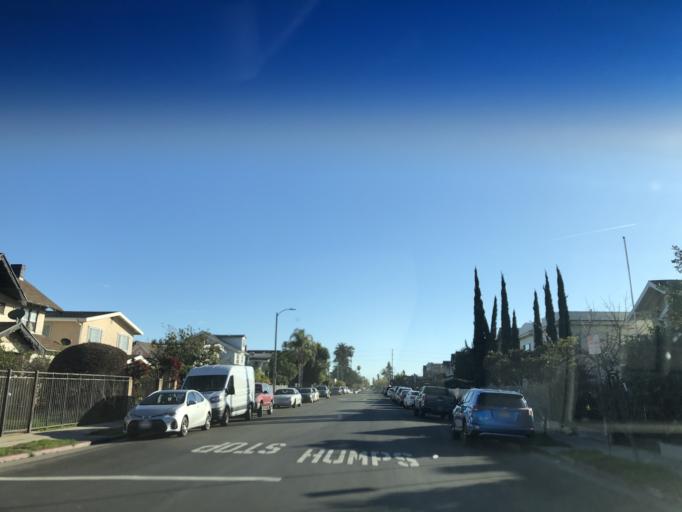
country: US
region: California
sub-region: Los Angeles County
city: Hollywood
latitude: 34.0455
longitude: -118.3226
